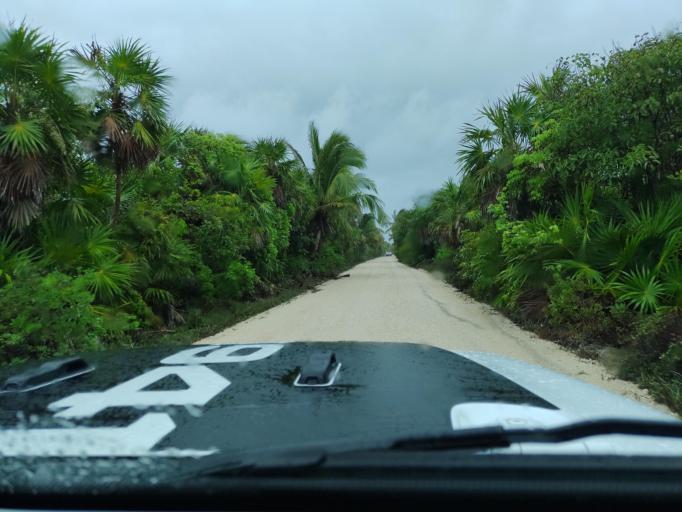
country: MX
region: Quintana Roo
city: Tulum
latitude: 19.9890
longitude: -87.4650
